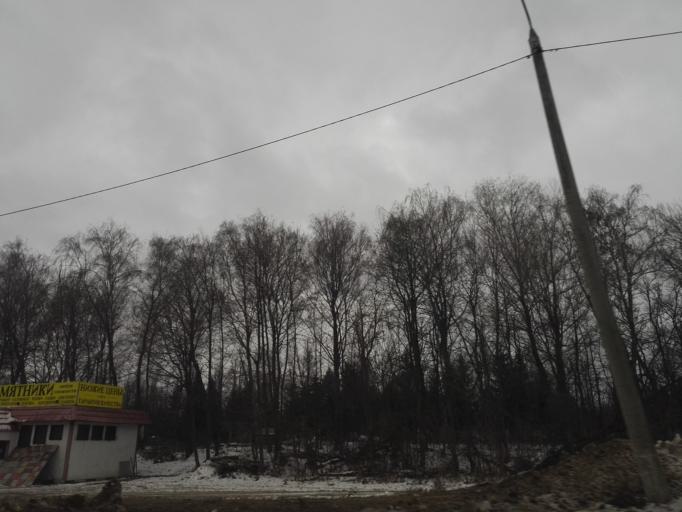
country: RU
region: Tula
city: Tula
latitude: 54.1518
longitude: 37.6394
